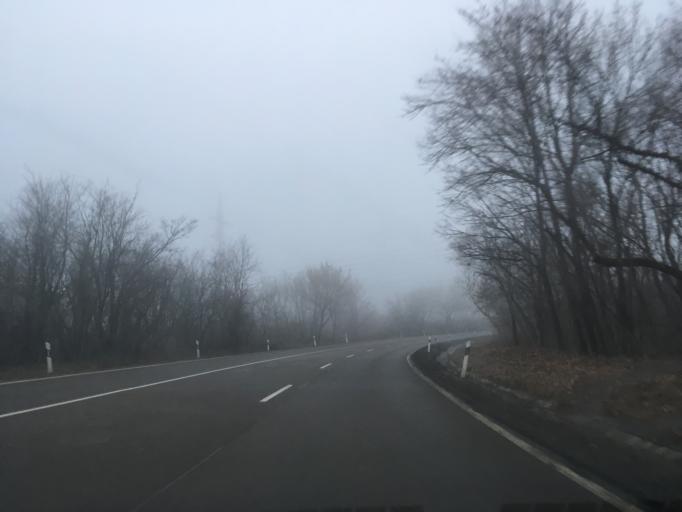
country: HU
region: Heves
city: Andornaktalya
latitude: 47.8627
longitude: 20.3793
